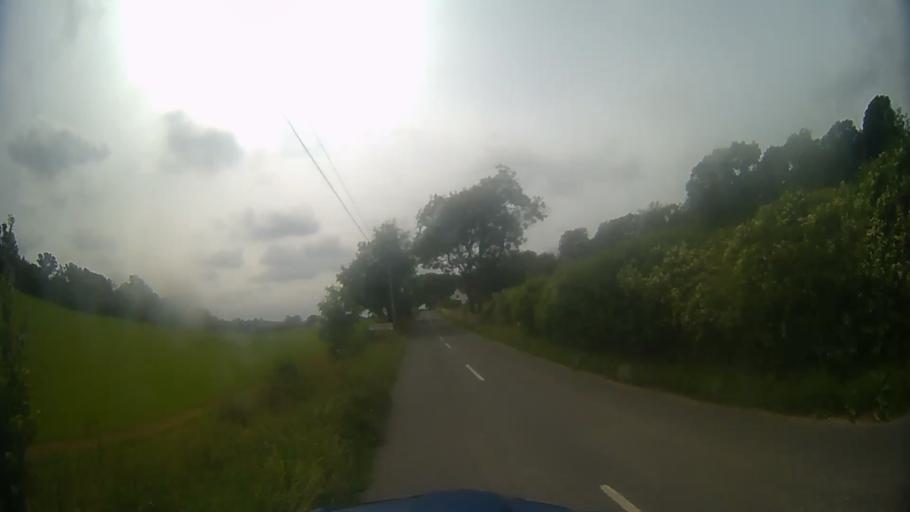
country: GB
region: England
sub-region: Hampshire
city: Overton
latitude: 51.2612
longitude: -1.3187
